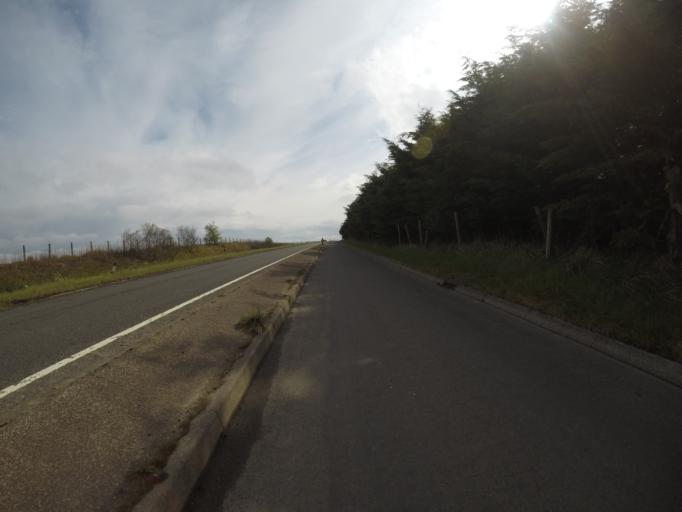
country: GB
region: Scotland
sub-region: East Renfrewshire
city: Newton Mearns
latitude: 55.7319
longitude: -4.3819
